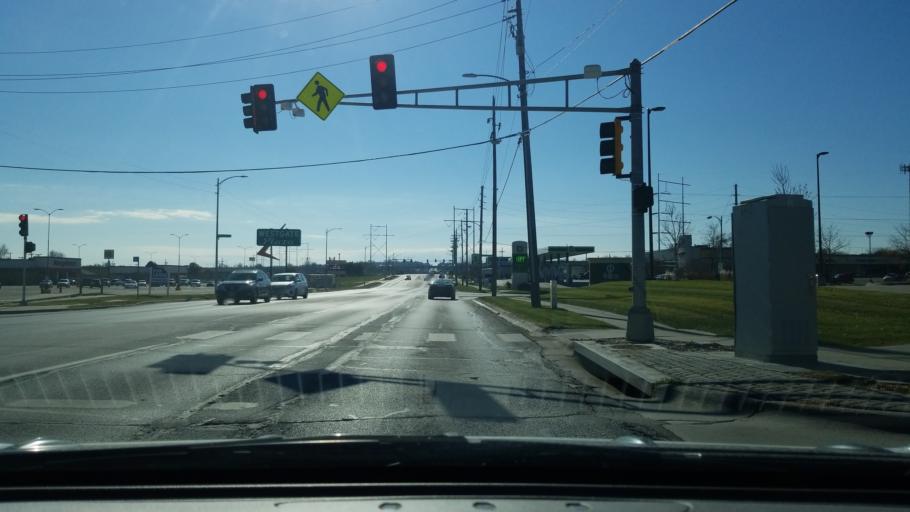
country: US
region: Nebraska
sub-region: Douglas County
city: Ralston
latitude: 41.2304
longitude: -96.0432
